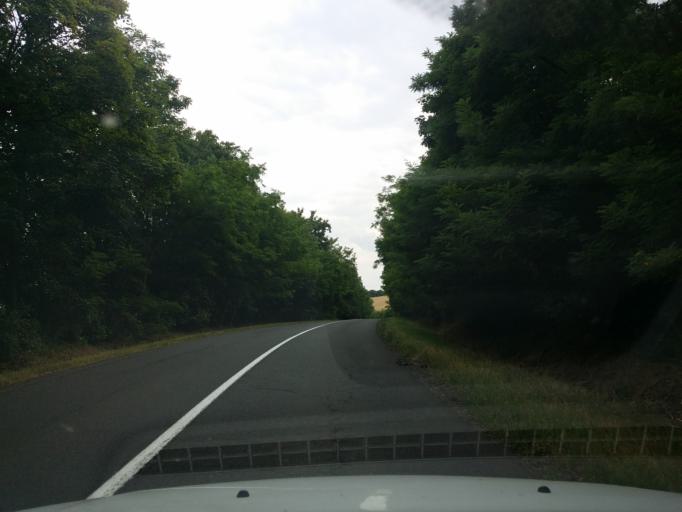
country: HU
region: Nograd
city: Bercel
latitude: 47.9343
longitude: 19.3676
